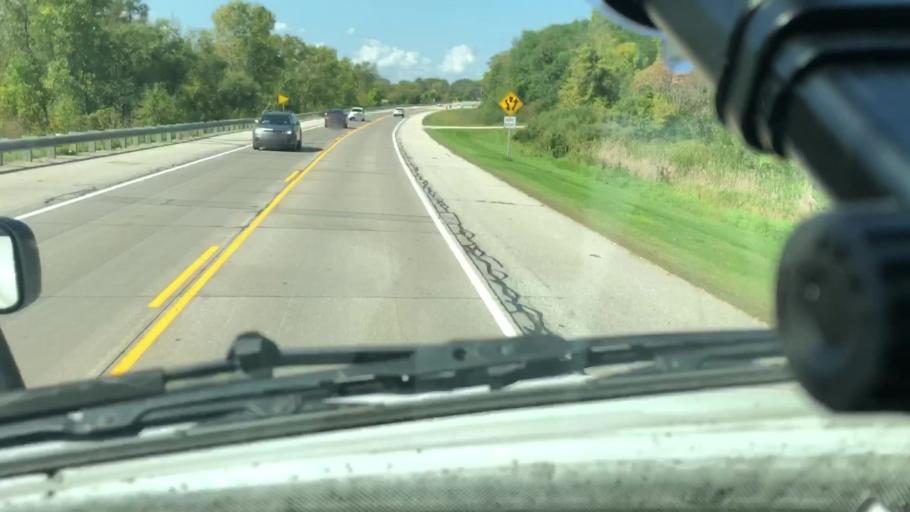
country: US
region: Minnesota
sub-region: Winona County
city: Winona
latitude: 44.0715
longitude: -91.6226
